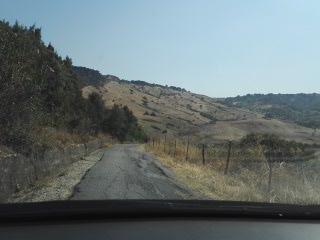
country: IT
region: Calabria
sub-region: Provincia di Reggio Calabria
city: Camini
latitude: 38.4419
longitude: 16.4670
